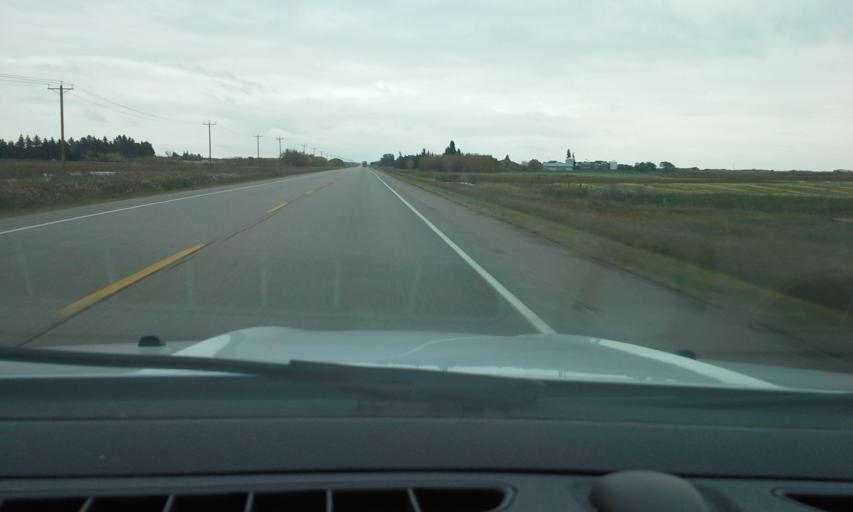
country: CA
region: Saskatchewan
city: Lloydminster
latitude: 53.2780
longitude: -109.8627
